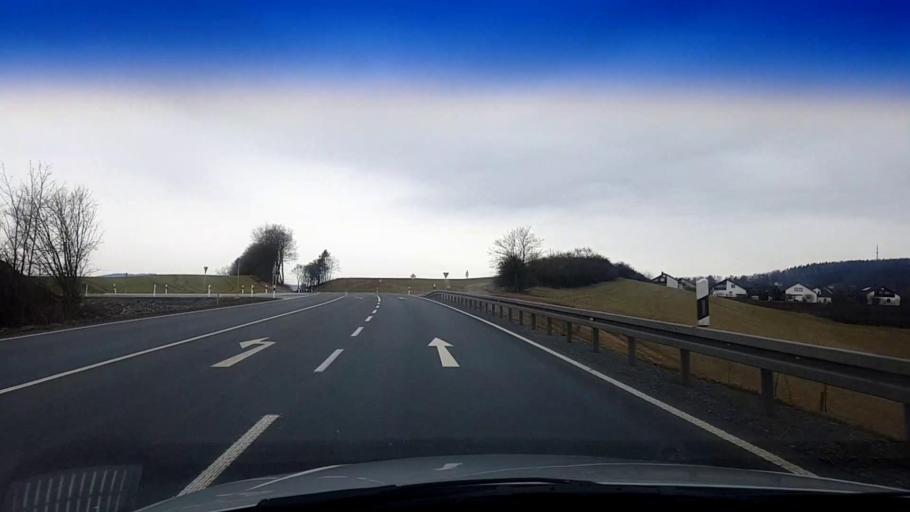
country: DE
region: Bavaria
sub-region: Upper Franconia
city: Kulmbach
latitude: 50.0833
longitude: 11.4627
